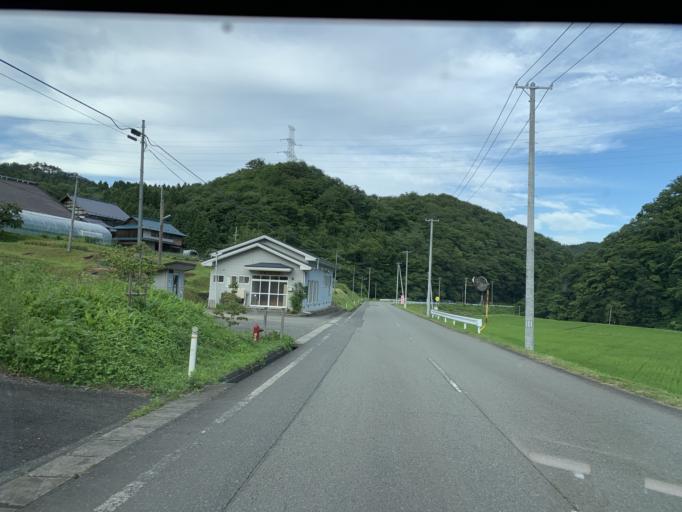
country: JP
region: Iwate
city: Ichinoseki
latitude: 38.9003
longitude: 140.9958
